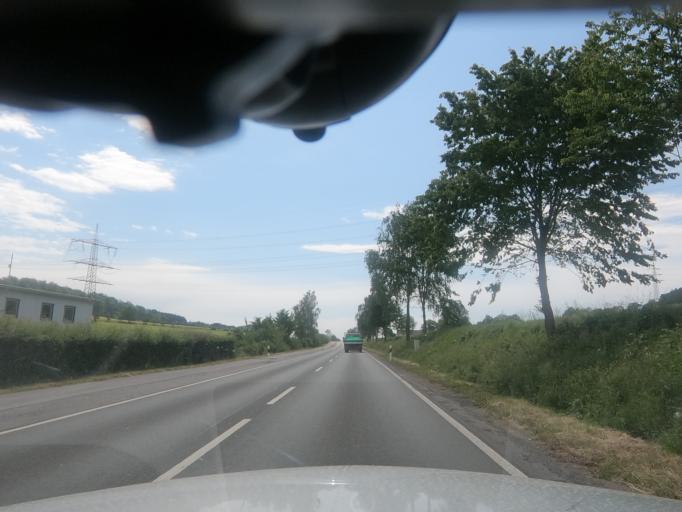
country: DE
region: North Rhine-Westphalia
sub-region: Regierungsbezirk Arnsberg
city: Sundern
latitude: 51.3228
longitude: 8.0354
